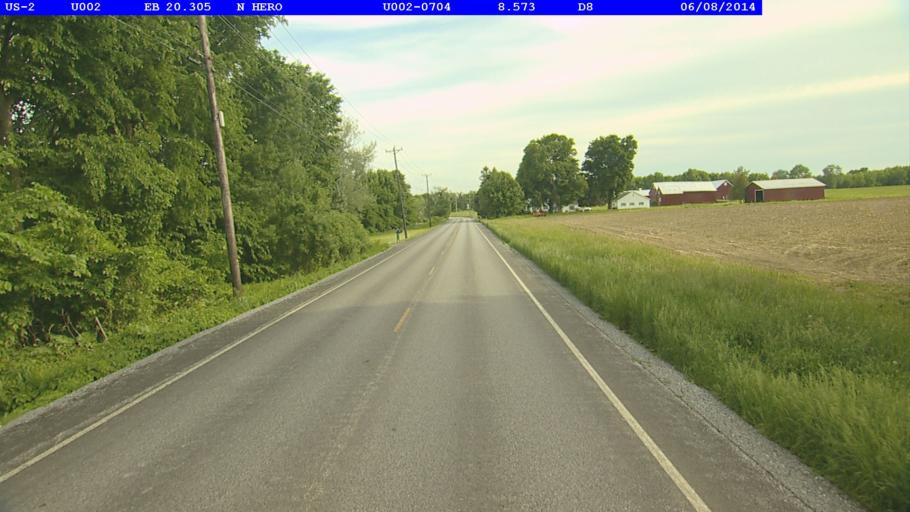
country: US
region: Vermont
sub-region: Grand Isle County
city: North Hero
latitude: 44.7763
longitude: -73.2939
